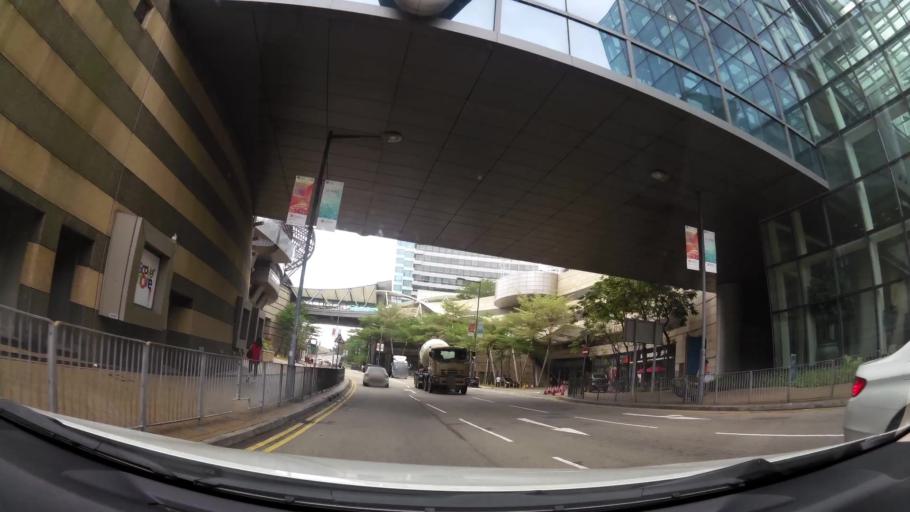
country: HK
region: Central and Western
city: Central
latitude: 22.2611
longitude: 114.1306
